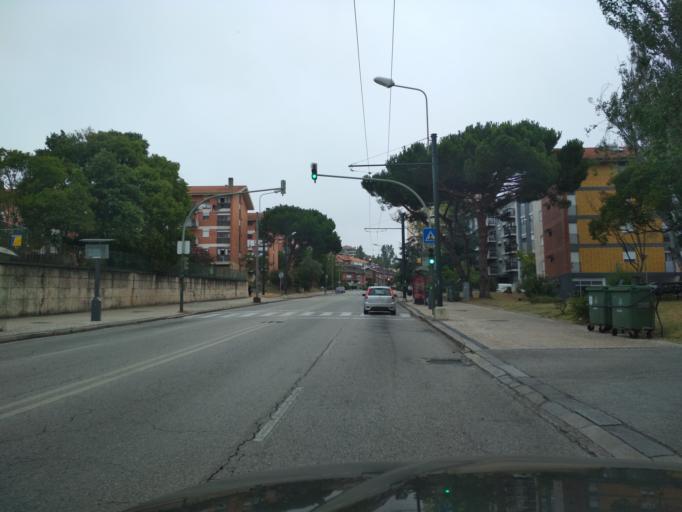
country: PT
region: Coimbra
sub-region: Coimbra
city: Coimbra
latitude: 40.2055
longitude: -8.4041
